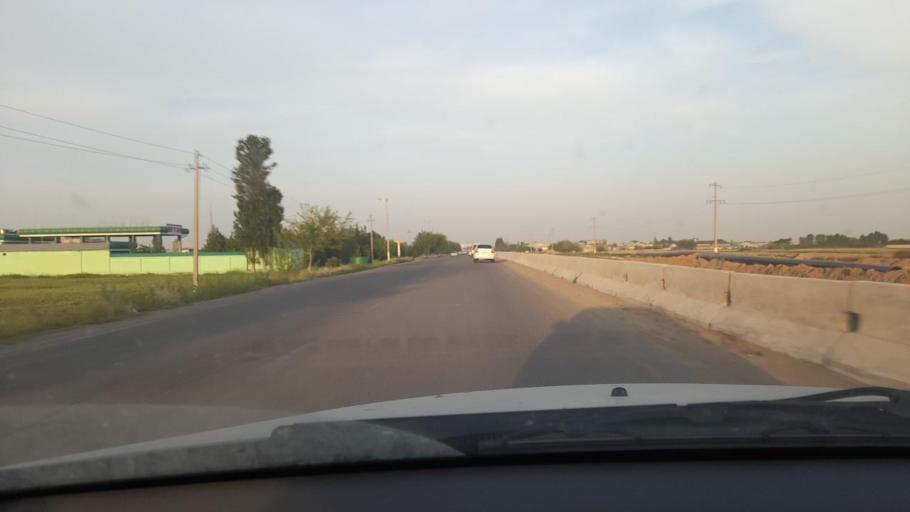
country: UZ
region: Sirdaryo
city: Guliston
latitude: 40.5078
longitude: 68.7385
